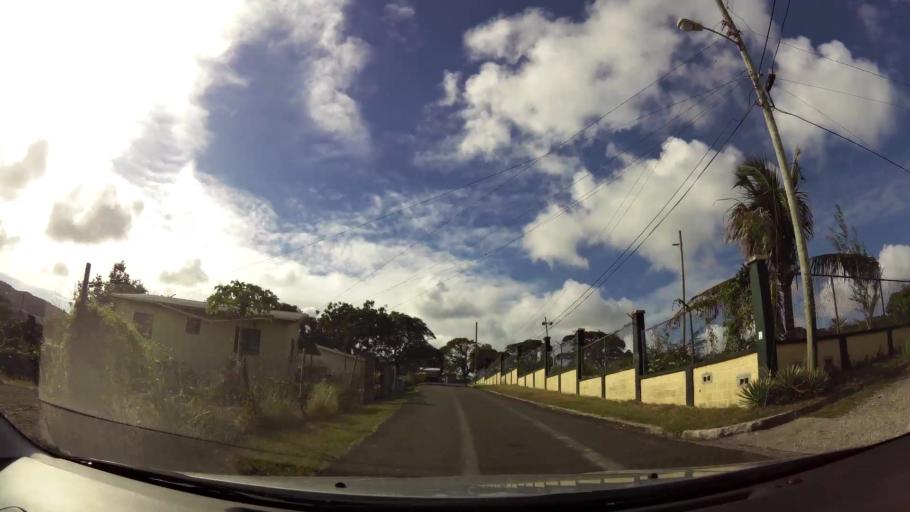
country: AG
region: Saint Peter
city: All Saints
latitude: 17.0514
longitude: -61.7991
